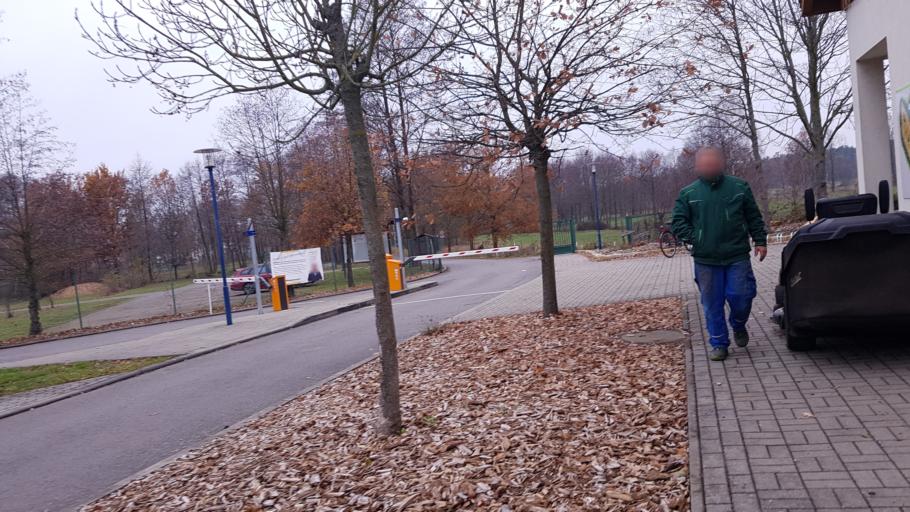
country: DE
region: Brandenburg
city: Ortrand
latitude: 51.3727
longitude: 13.7794
